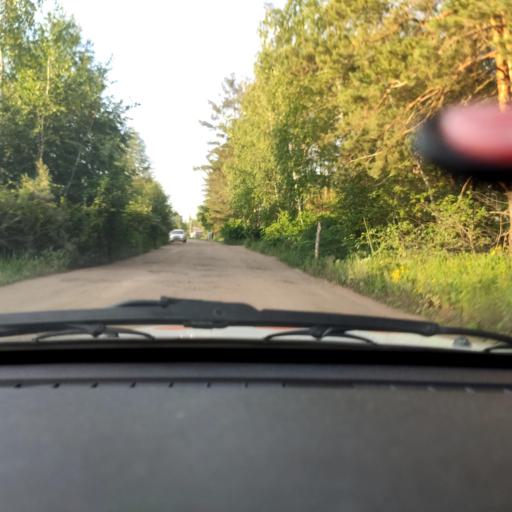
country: RU
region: Voronezj
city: Podgornoye
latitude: 51.8359
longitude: 39.1987
